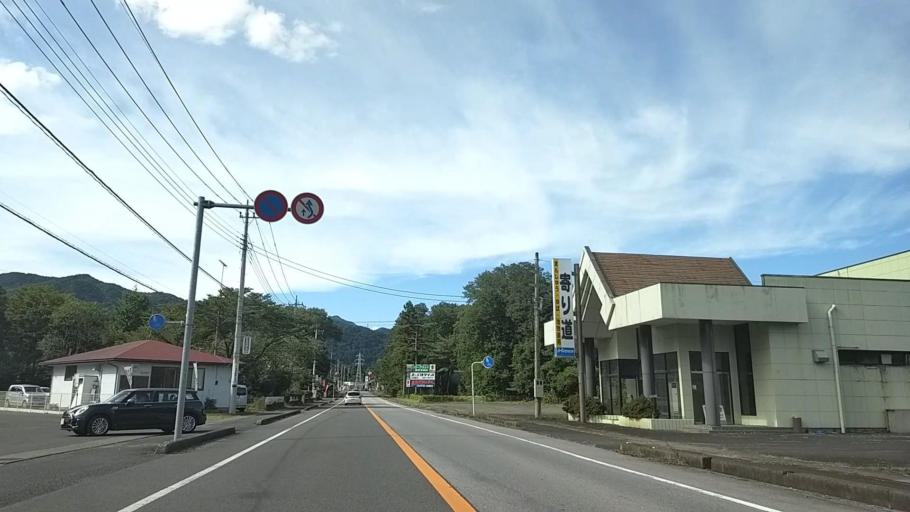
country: JP
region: Tochigi
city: Imaichi
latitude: 36.7804
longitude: 139.7050
